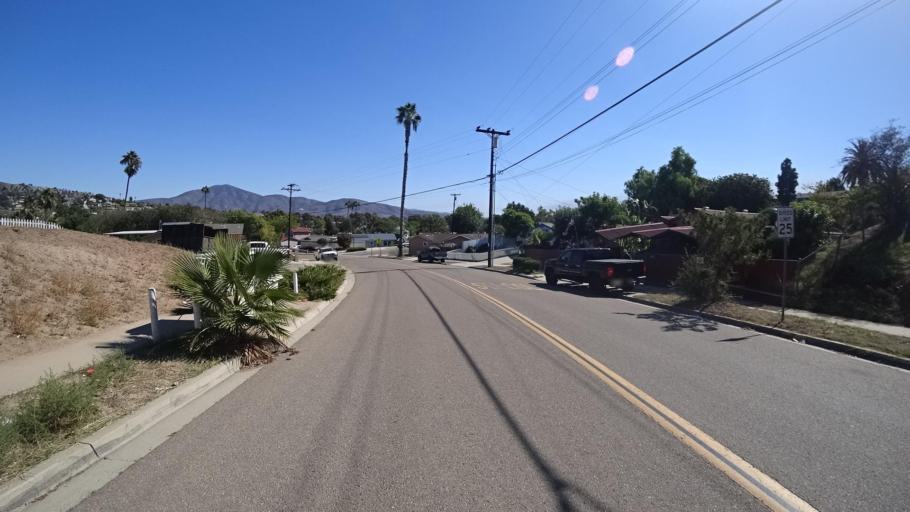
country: US
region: California
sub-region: San Diego County
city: La Presa
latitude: 32.7202
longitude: -117.0188
